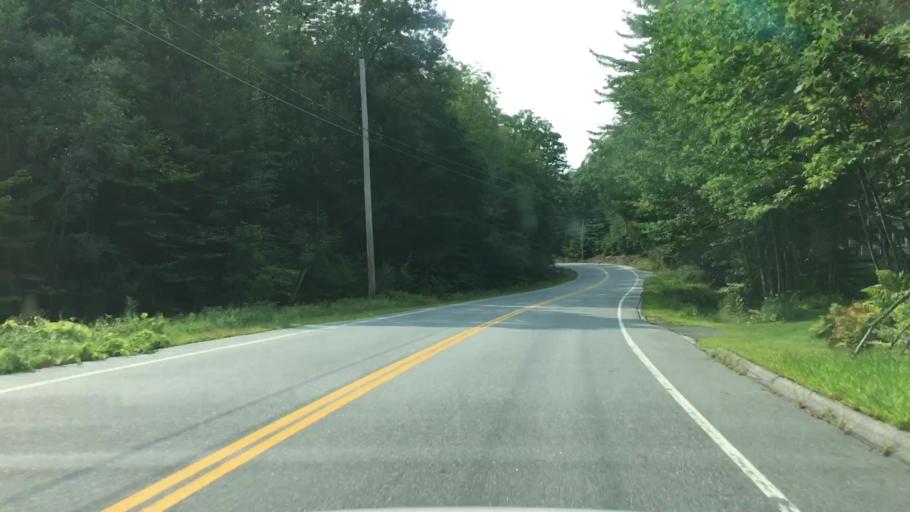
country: US
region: Maine
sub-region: Oxford County
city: Buckfield
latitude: 44.2710
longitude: -70.3989
